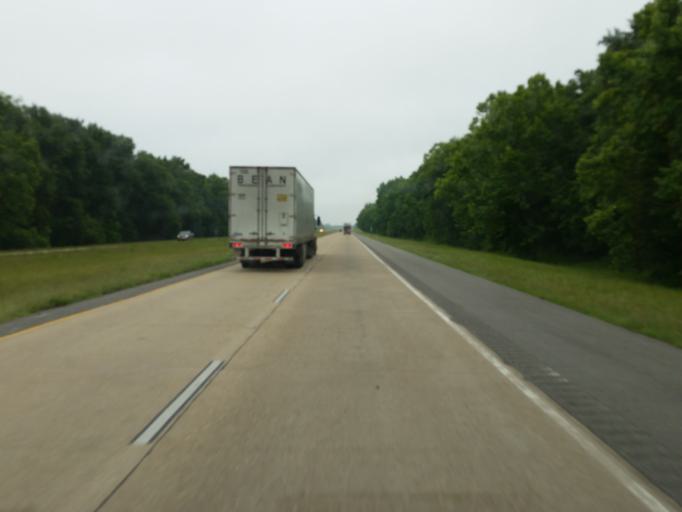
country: US
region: Louisiana
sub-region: Madison Parish
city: Tallulah
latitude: 32.3710
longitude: -91.1427
